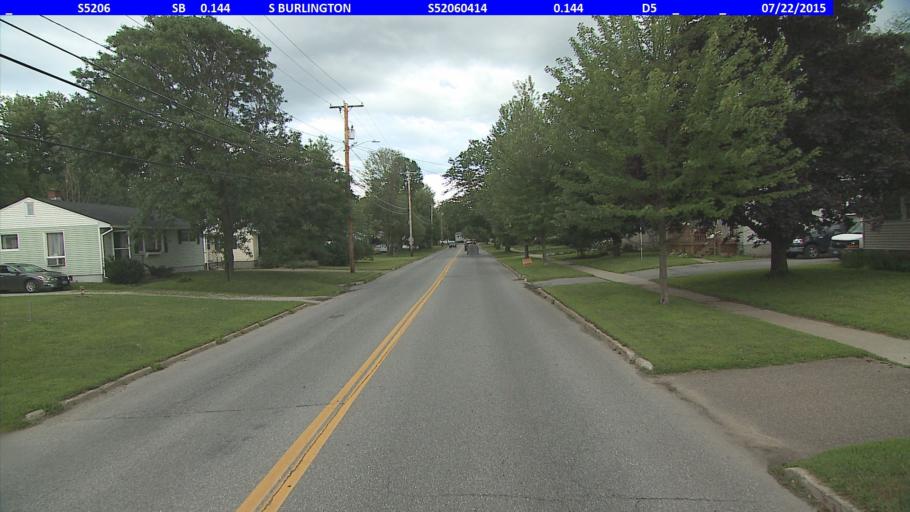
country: US
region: Vermont
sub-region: Chittenden County
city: South Burlington
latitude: 44.4727
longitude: -73.1642
